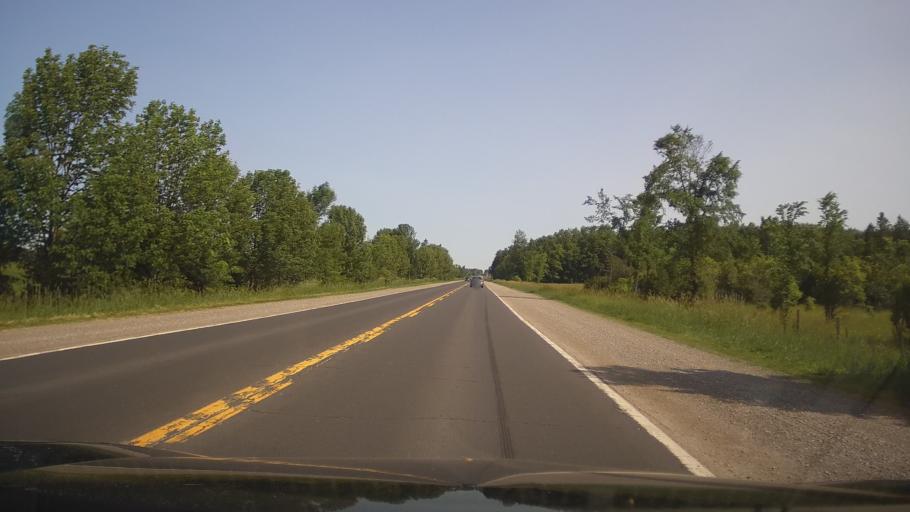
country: CA
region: Ontario
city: Omemee
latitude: 44.3156
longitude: -78.6806
